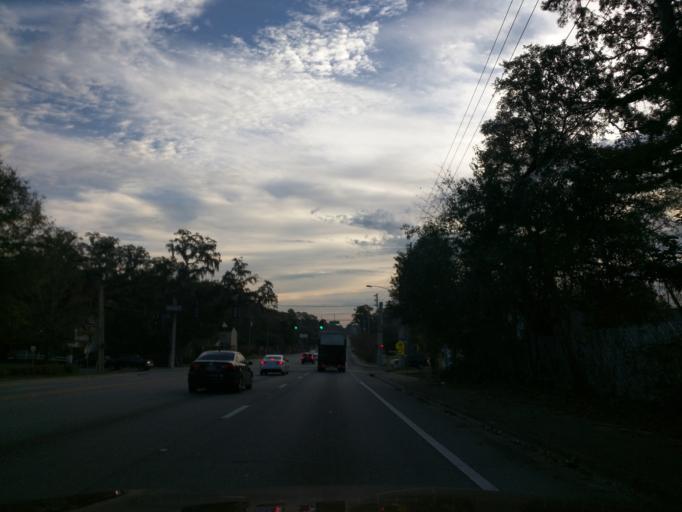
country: US
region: Florida
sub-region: Leon County
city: Tallahassee
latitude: 30.4636
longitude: -84.2926
